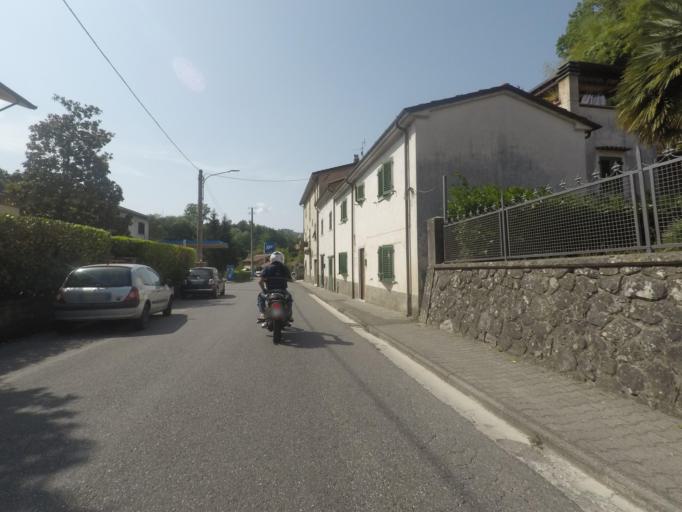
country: IT
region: Tuscany
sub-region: Provincia di Massa-Carrara
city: Casola in Lunigiana
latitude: 44.1666
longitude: 10.1228
